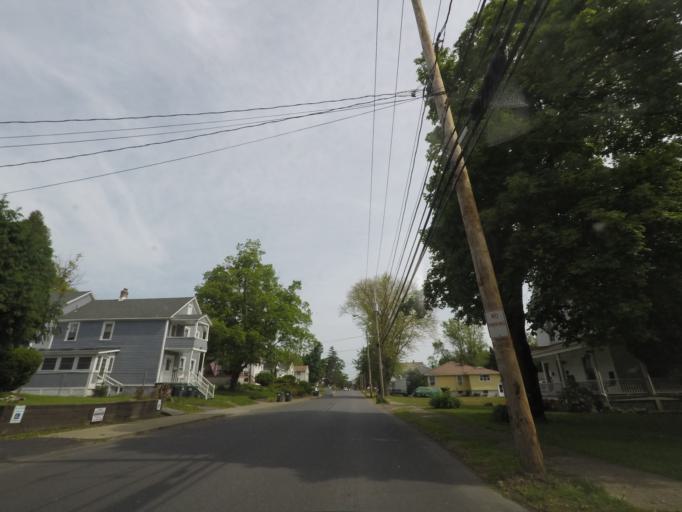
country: US
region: New York
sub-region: Saratoga County
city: Mechanicville
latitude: 42.8925
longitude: -73.6879
